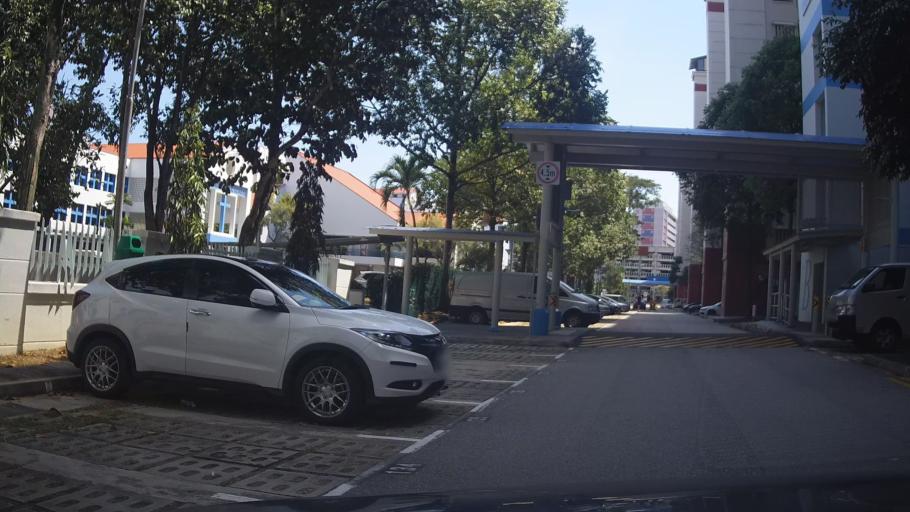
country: MY
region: Johor
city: Kampung Pasir Gudang Baru
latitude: 1.3744
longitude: 103.9545
